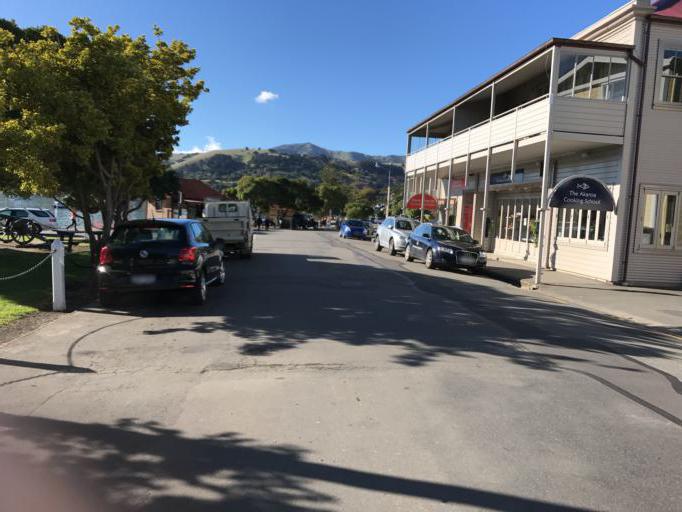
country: NZ
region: Canterbury
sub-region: Christchurch City
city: Christchurch
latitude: -43.8096
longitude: 172.9613
